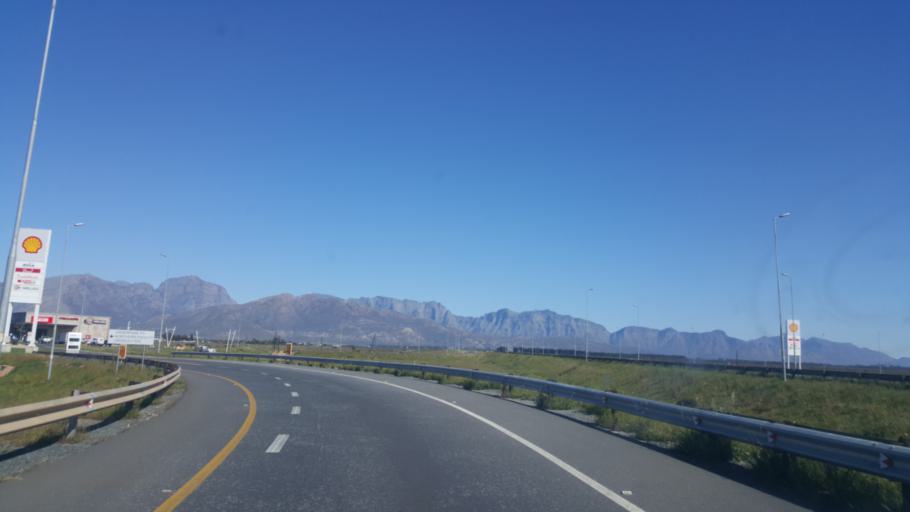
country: ZA
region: Western Cape
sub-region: Cape Winelands District Municipality
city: Worcester
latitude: -33.6349
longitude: 19.3603
